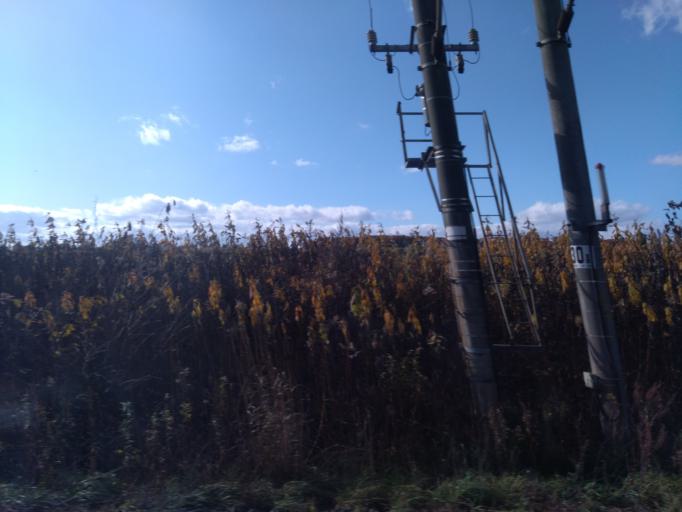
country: JP
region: Hokkaido
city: Kitahiroshima
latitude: 42.9608
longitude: 141.5688
